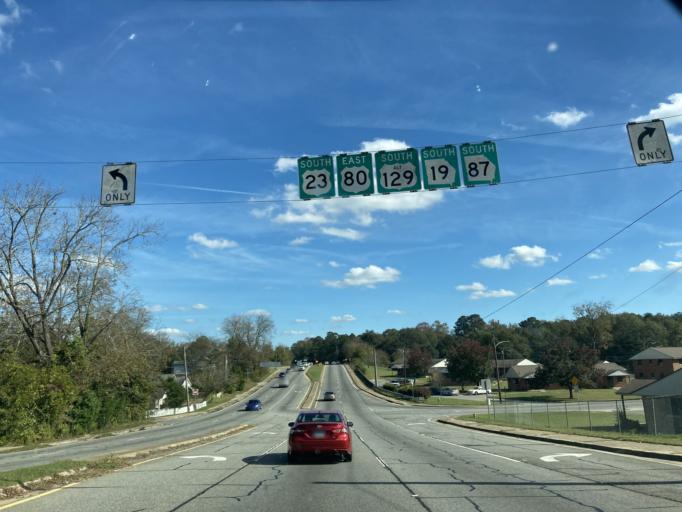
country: US
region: Georgia
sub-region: Bibb County
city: Macon
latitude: 32.8481
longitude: -83.6084
